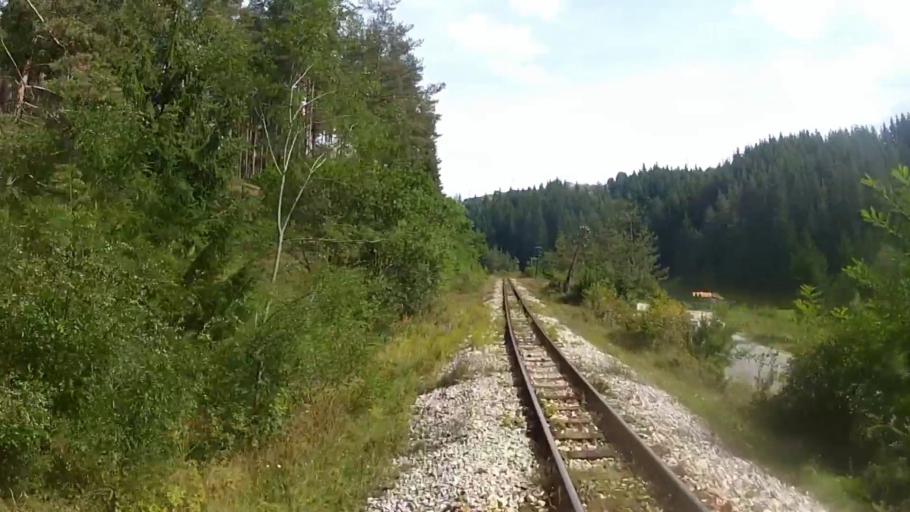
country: BG
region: Blagoevgrad
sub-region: Obshtina Yakoruda
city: Yakoruda
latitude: 42.0373
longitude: 23.8030
